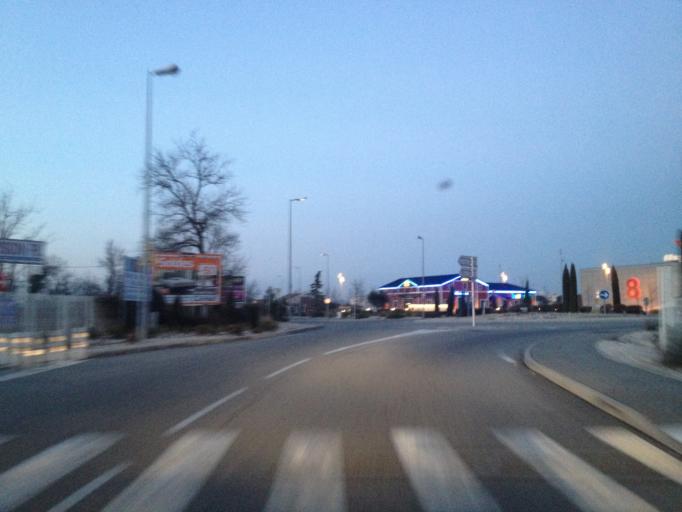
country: FR
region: Provence-Alpes-Cote d'Azur
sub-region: Departement du Vaucluse
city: Le Pontet
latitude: 43.9785
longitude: 4.8718
